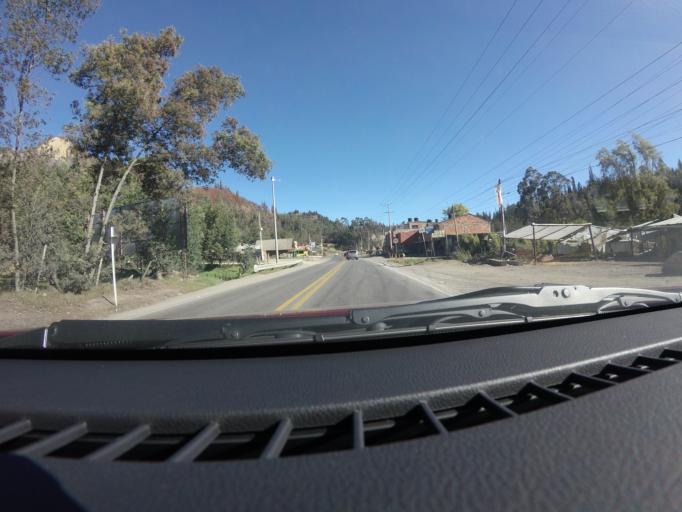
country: CO
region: Cundinamarca
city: Sutatausa
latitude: 5.2497
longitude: -73.8549
